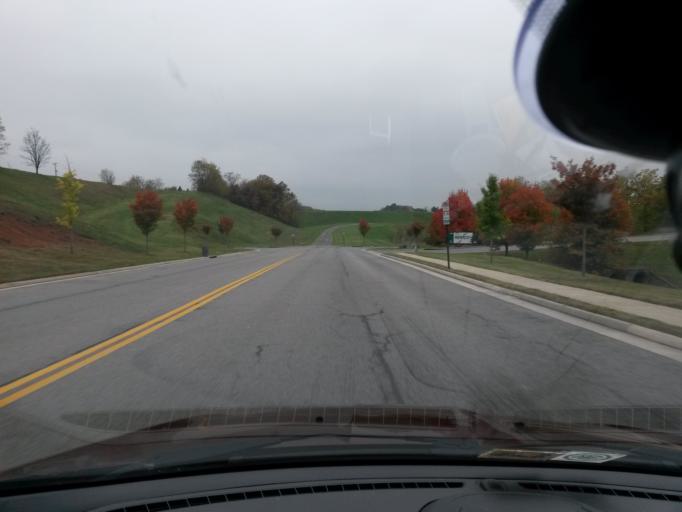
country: US
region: Virginia
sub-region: Roanoke County
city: Vinton
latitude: 37.3056
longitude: -79.9062
